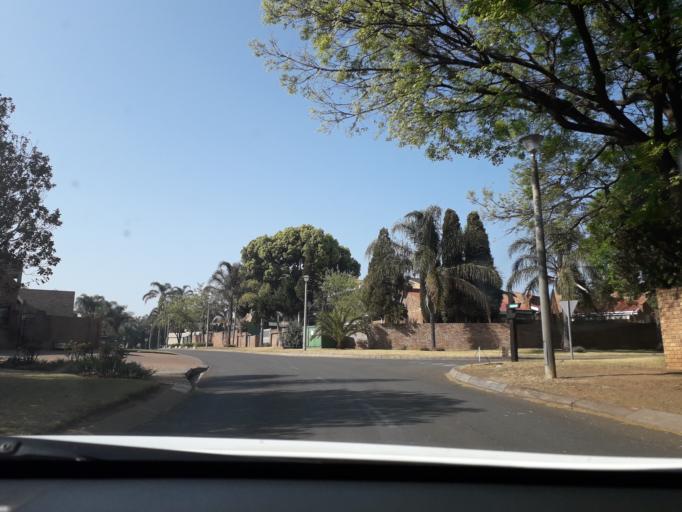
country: ZA
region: Gauteng
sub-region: Ekurhuleni Metropolitan Municipality
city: Tembisa
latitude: -26.0664
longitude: 28.2479
